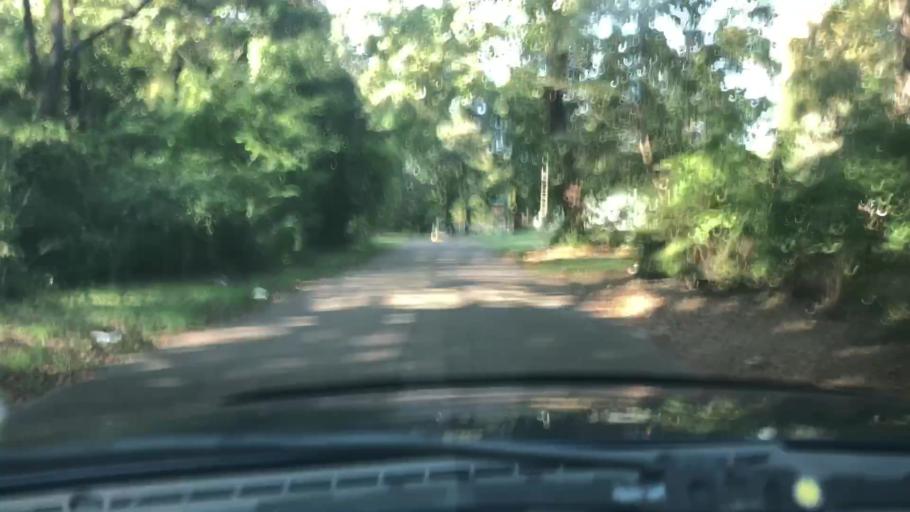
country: US
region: Texas
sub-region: Bowie County
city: Texarkana
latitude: 33.4160
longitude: -94.0627
